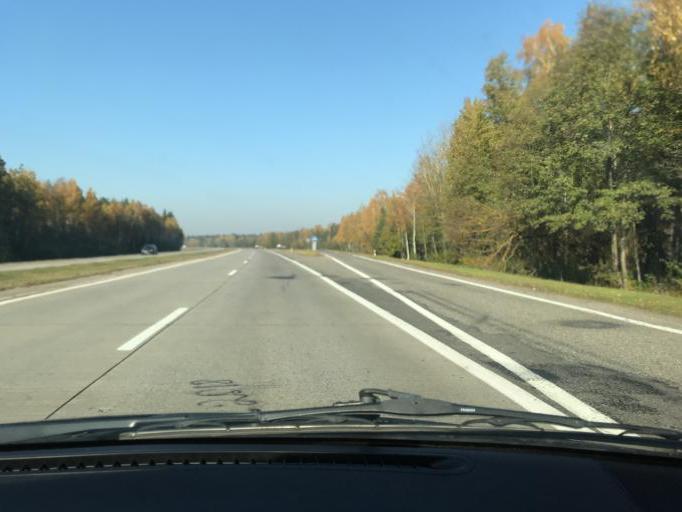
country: BY
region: Minsk
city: Uzda
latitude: 53.3679
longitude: 27.5074
